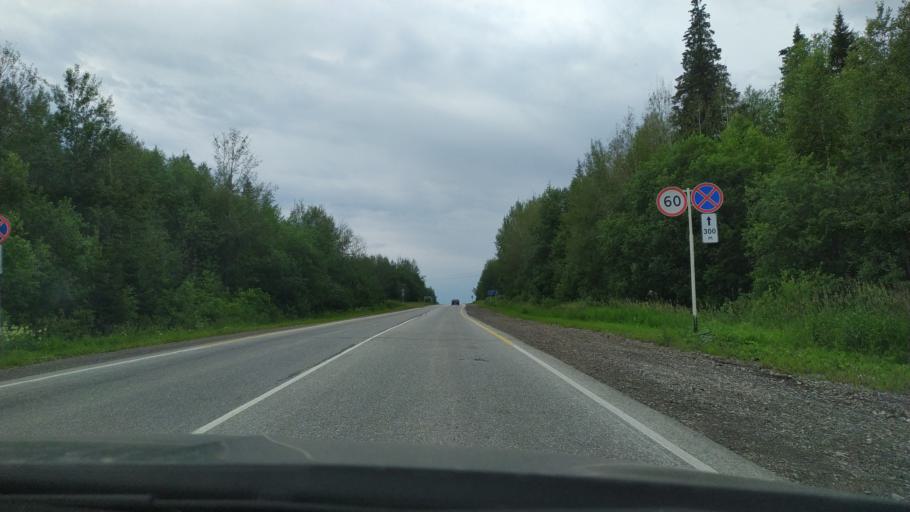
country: RU
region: Perm
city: Chusovoy
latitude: 58.3868
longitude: 57.9008
